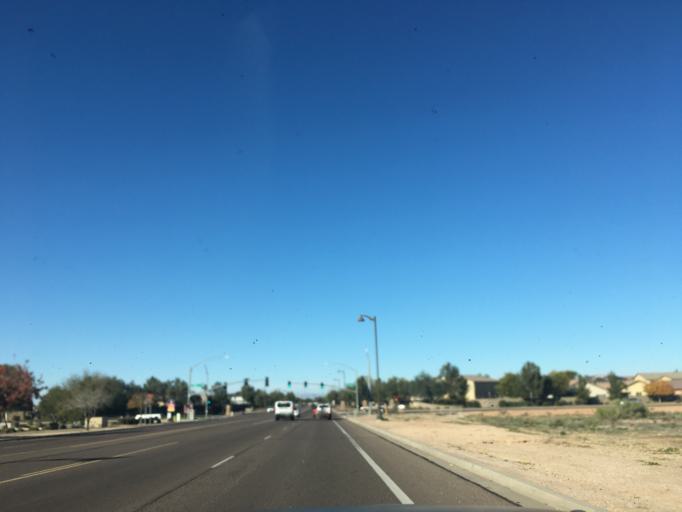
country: US
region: Arizona
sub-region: Pinal County
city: Maricopa
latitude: 33.0426
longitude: -112.0130
